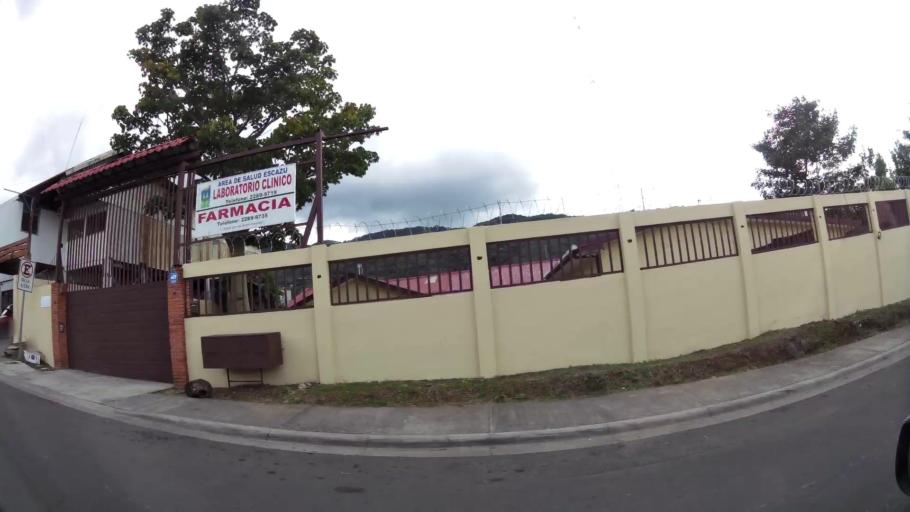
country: CR
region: San Jose
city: Escazu
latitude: 9.9213
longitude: -84.1454
